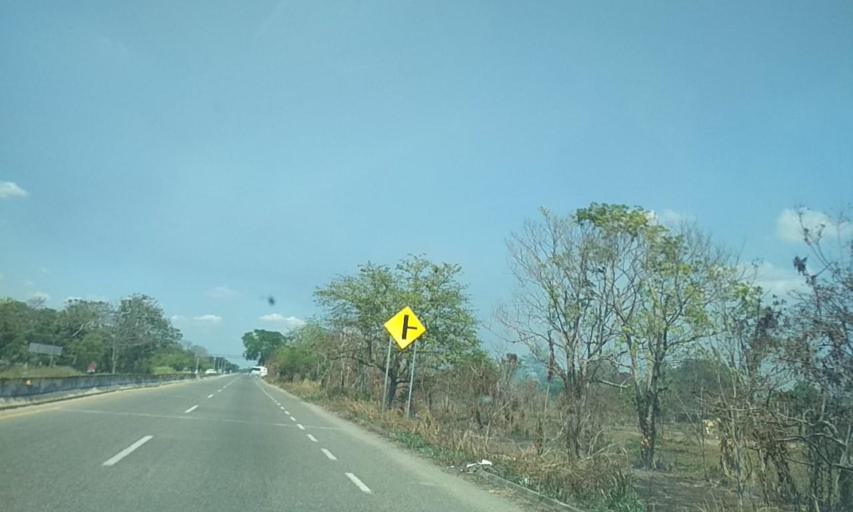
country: MX
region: Tabasco
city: Huimanguillo
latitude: 17.8588
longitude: -93.3941
